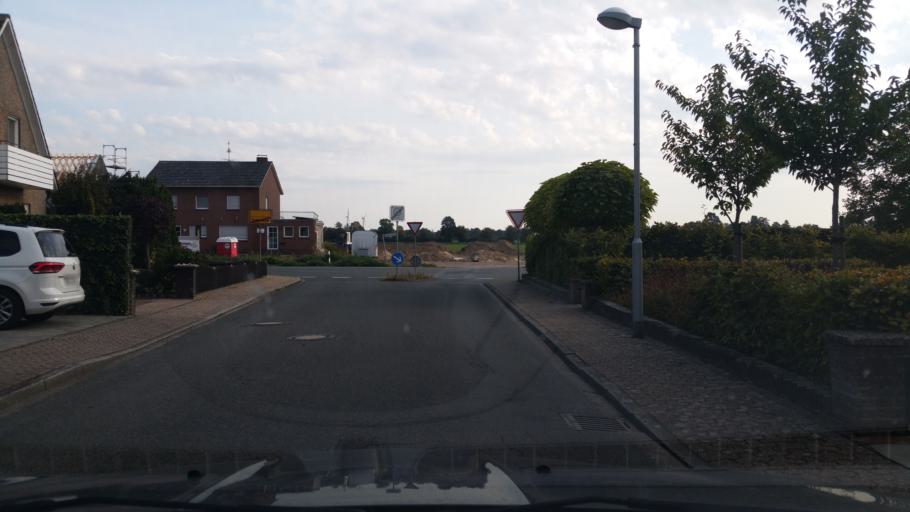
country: DE
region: North Rhine-Westphalia
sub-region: Regierungsbezirk Munster
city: Isselburg
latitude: 51.8575
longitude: 6.4984
